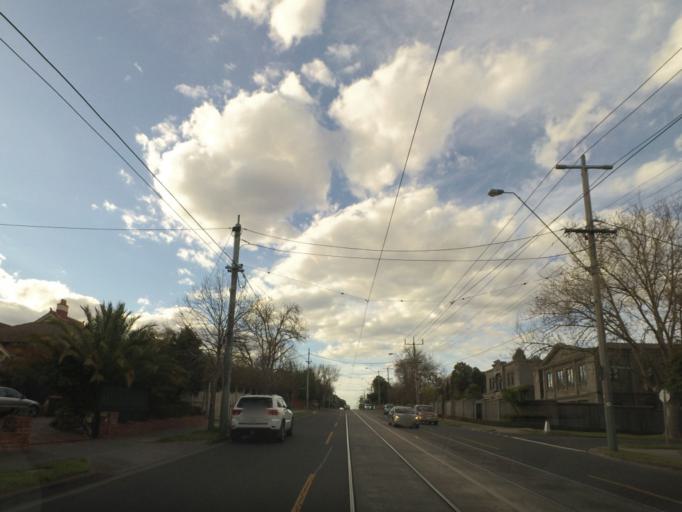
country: AU
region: Victoria
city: Glenferrie
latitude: -37.8395
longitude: 145.0551
